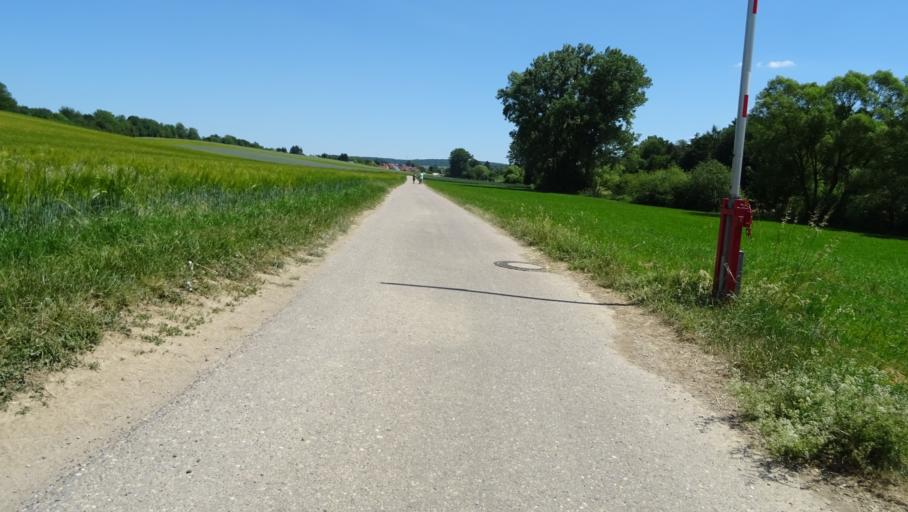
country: DE
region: Baden-Wuerttemberg
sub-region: Karlsruhe Region
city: Aglasterhausen
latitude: 49.3427
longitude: 9.0097
